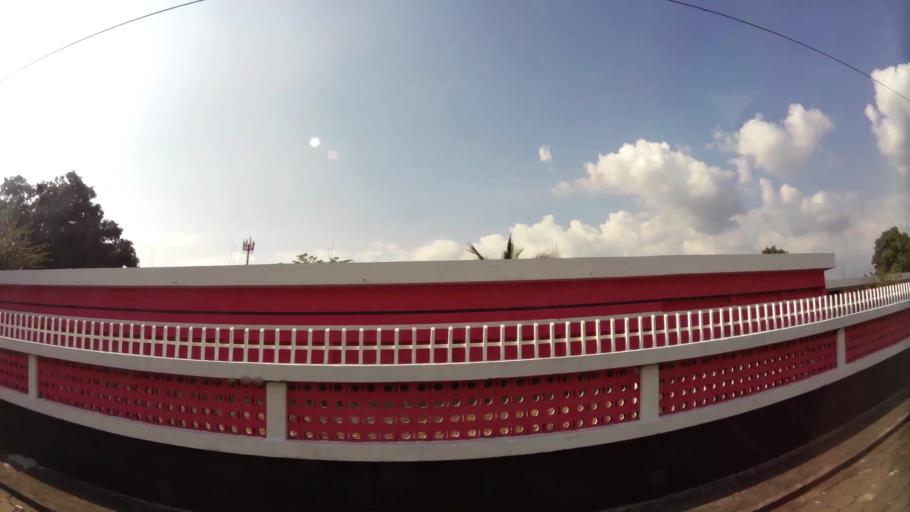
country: GT
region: Retalhuleu
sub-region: Municipio de Retalhuleu
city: Retalhuleu
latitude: 14.5395
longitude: -91.6860
